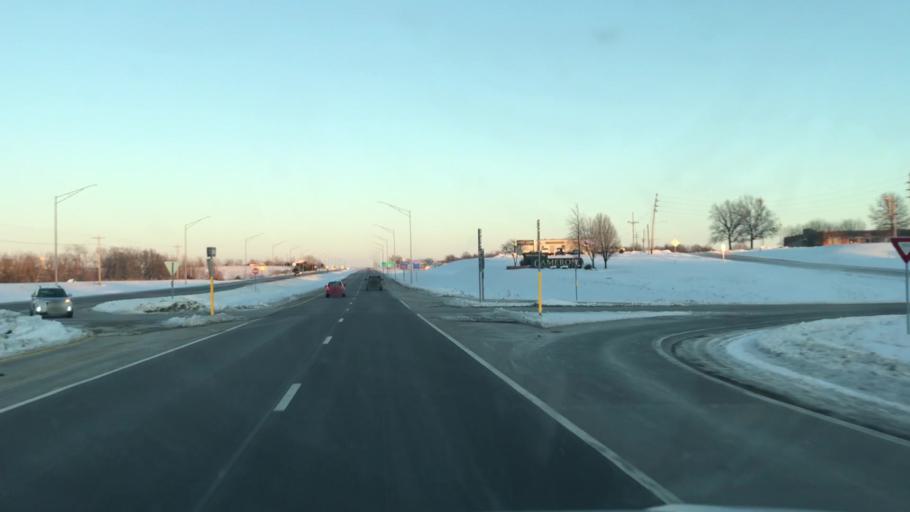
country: US
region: Missouri
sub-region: Clinton County
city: Cameron
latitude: 39.7540
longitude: -94.2526
